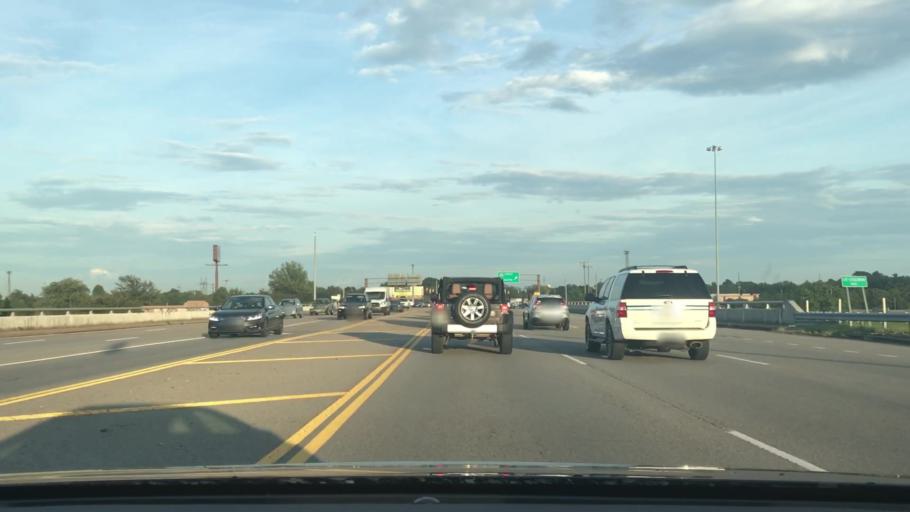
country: US
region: Tennessee
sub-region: Davidson County
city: Oak Hill
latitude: 36.0826
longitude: -86.7649
